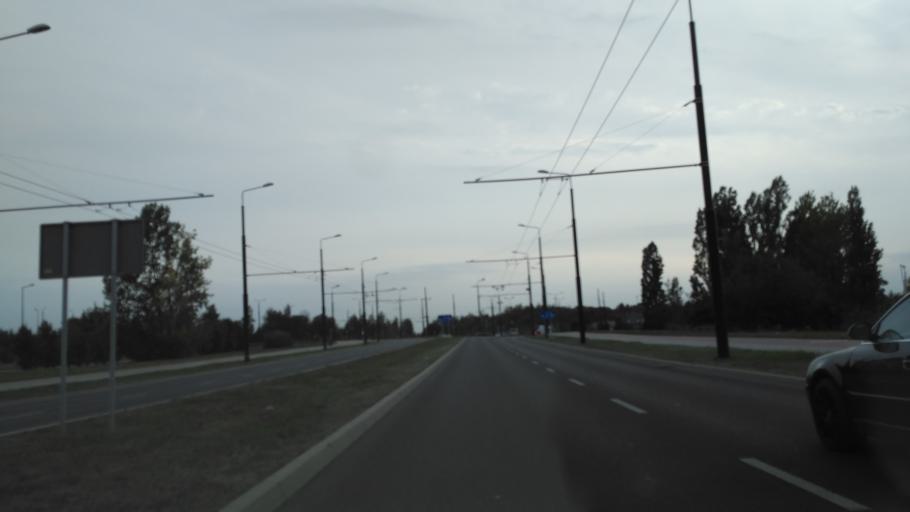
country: PL
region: Lublin Voivodeship
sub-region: Powiat lubelski
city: Jakubowice Murowane
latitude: 51.2250
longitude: 22.6156
